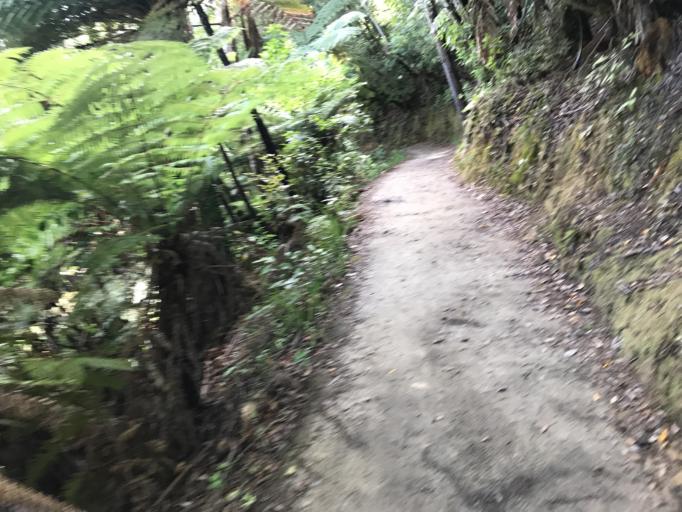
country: NZ
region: Marlborough
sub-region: Marlborough District
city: Picton
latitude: -41.2630
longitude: 173.9272
